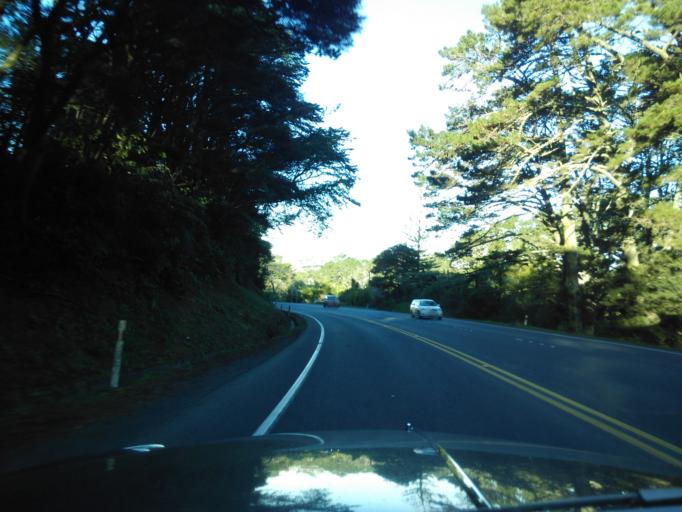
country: NZ
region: Auckland
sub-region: Auckland
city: Rothesay Bay
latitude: -36.7221
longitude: 174.6826
